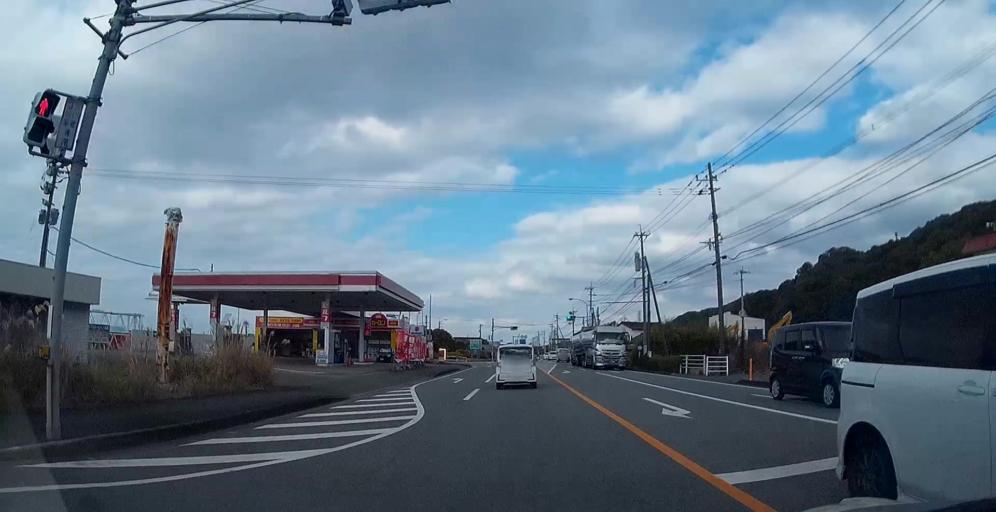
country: JP
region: Kumamoto
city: Yatsushiro
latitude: 32.4605
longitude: 130.6013
